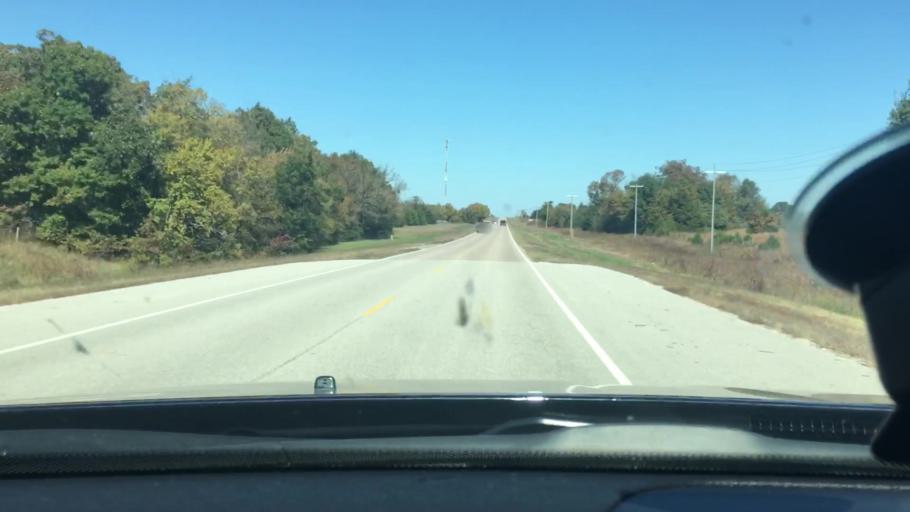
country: US
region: Oklahoma
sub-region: Johnston County
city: Tishomingo
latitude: 34.4225
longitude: -96.6359
